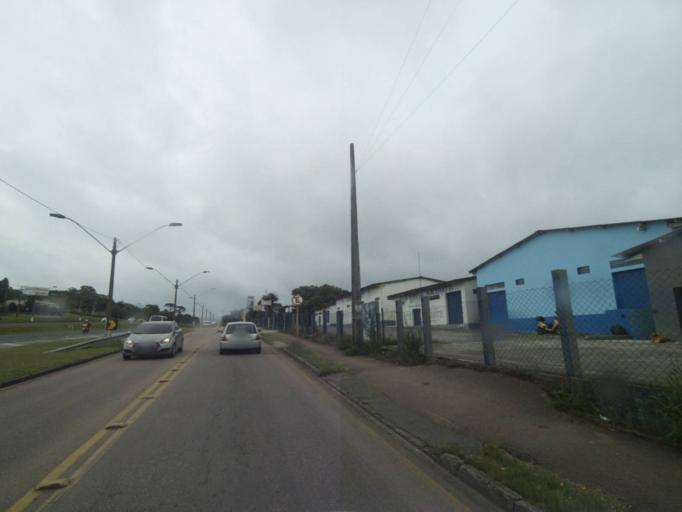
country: BR
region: Parana
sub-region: Curitiba
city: Curitiba
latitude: -25.4303
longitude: -49.3371
